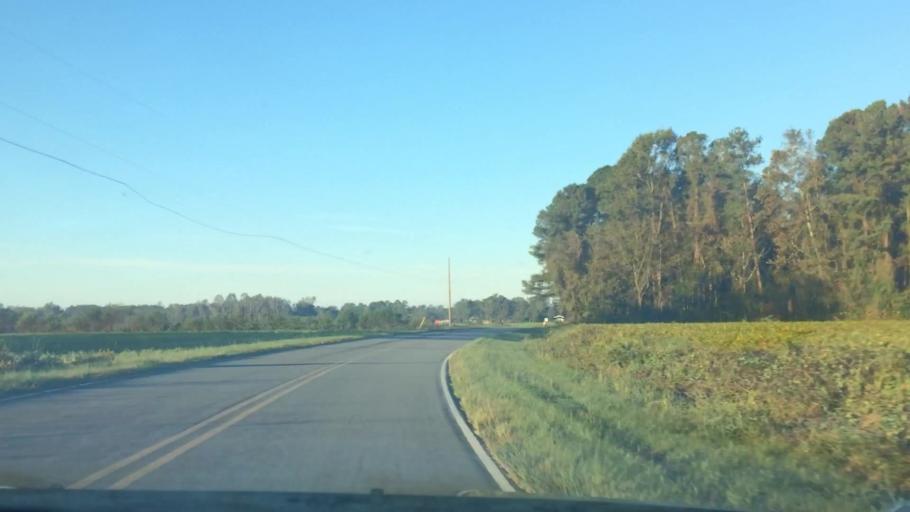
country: US
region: North Carolina
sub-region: Pitt County
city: Grifton
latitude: 35.3831
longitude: -77.4124
